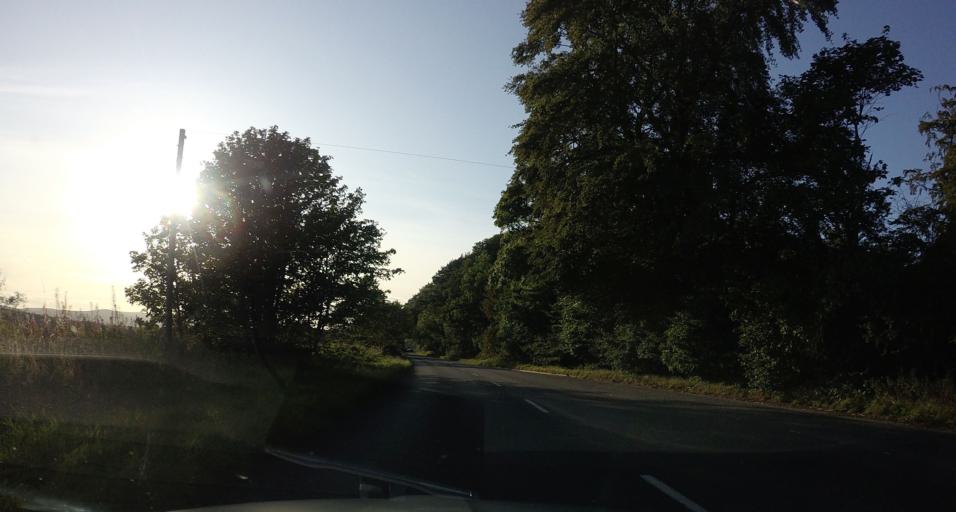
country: GB
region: Scotland
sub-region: Aberdeenshire
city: Westhill
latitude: 57.1550
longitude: -2.3229
